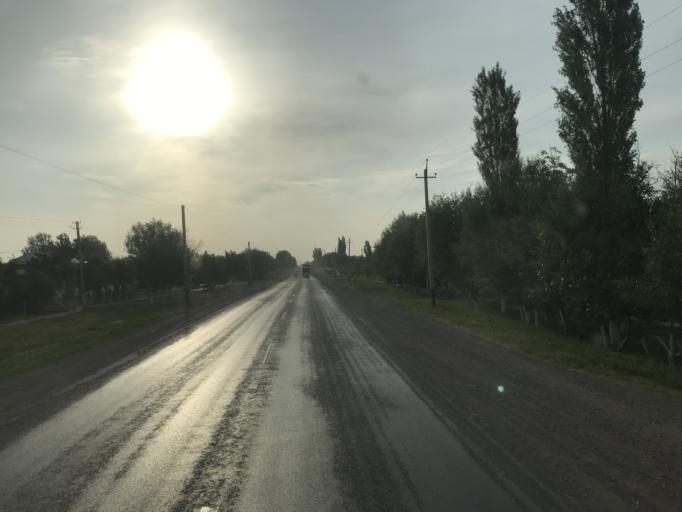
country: UZ
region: Toshkent
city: Salor
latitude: 41.4937
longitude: 69.3096
